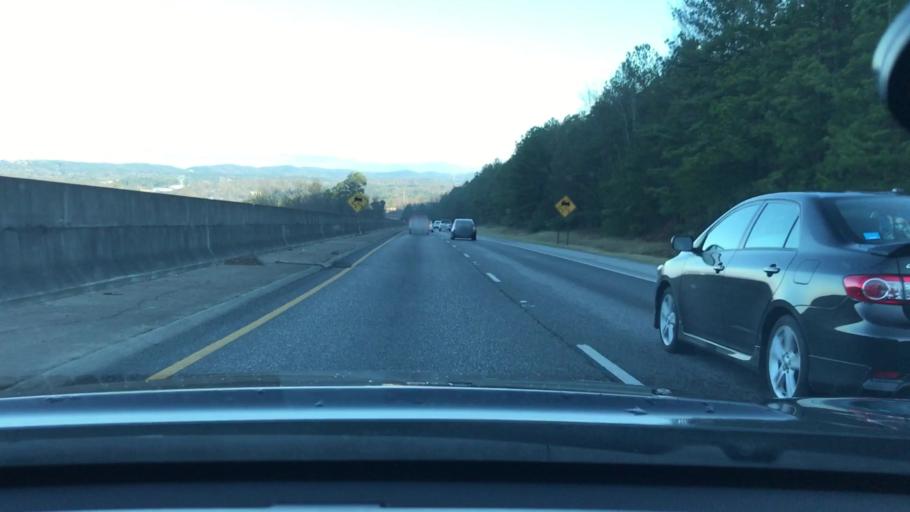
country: US
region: Alabama
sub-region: Shelby County
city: Meadowbrook
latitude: 33.3952
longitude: -86.6648
